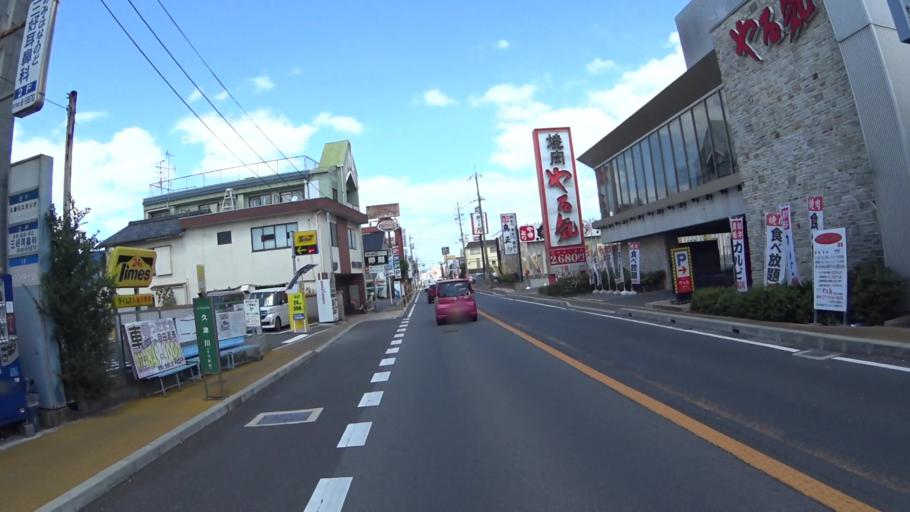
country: JP
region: Kyoto
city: Uji
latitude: 34.8651
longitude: 135.7770
